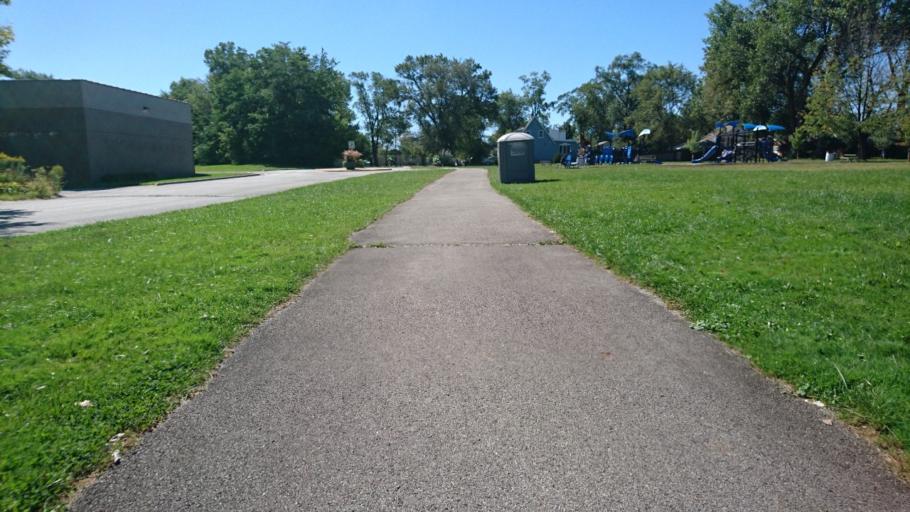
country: US
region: Illinois
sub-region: Cook County
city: Lansing
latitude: 41.5680
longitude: -87.5371
